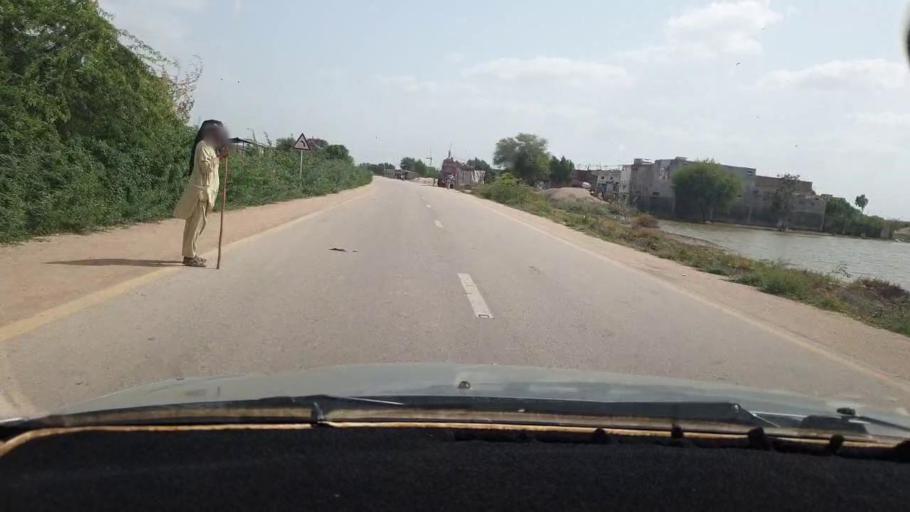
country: PK
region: Sindh
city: Naukot
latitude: 24.9776
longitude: 69.2947
